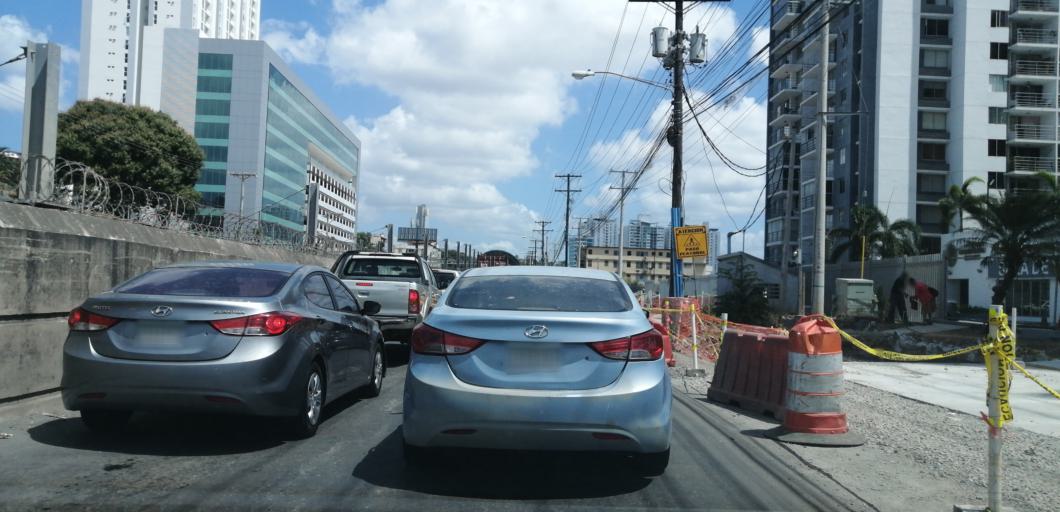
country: PA
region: Panama
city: Panama
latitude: 9.0118
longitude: -79.5176
